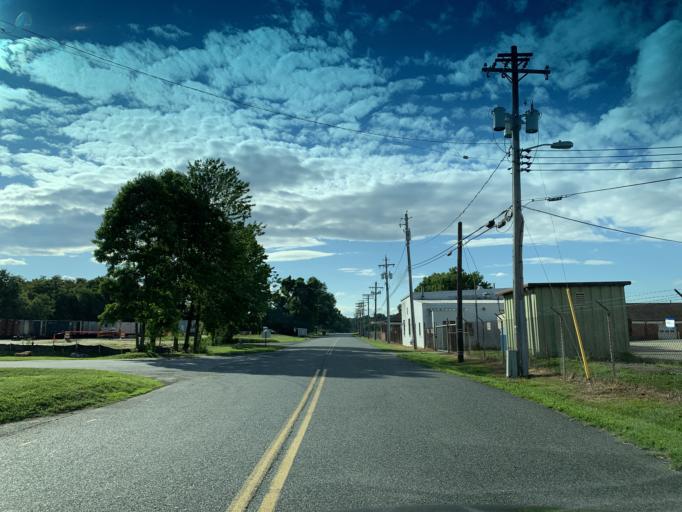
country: US
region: Maryland
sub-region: Harford County
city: Havre de Grace
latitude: 39.5325
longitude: -76.1062
